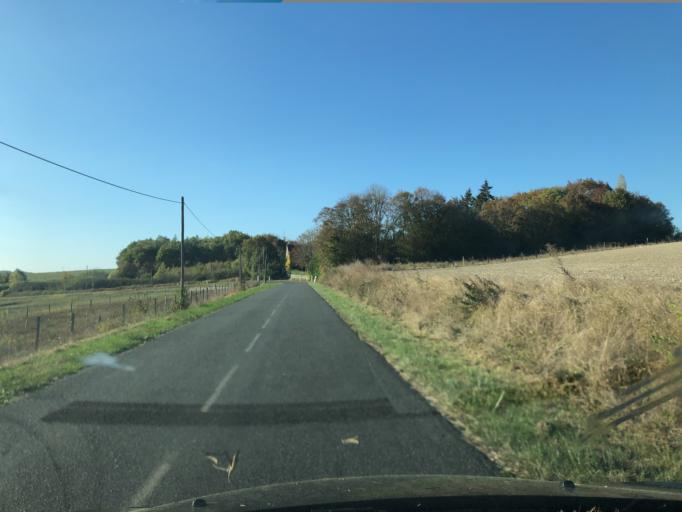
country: FR
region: Centre
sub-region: Departement d'Indre-et-Loire
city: Neuvy-le-Roi
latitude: 47.6670
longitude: 0.6317
